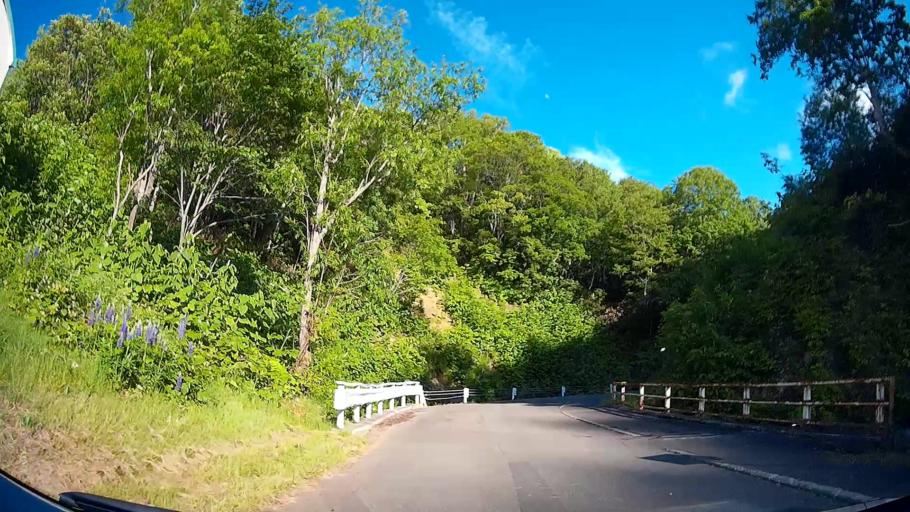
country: JP
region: Hokkaido
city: Otaru
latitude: 42.9810
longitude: 141.0412
